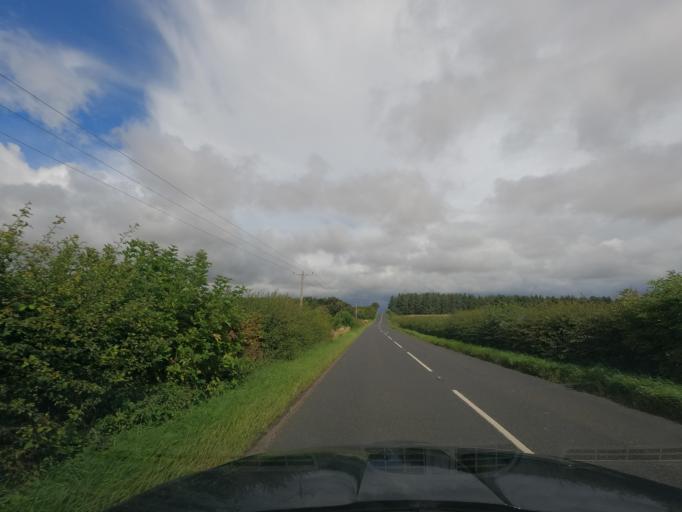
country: GB
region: England
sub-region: Northumberland
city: Ancroft
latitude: 55.6694
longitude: -2.0005
